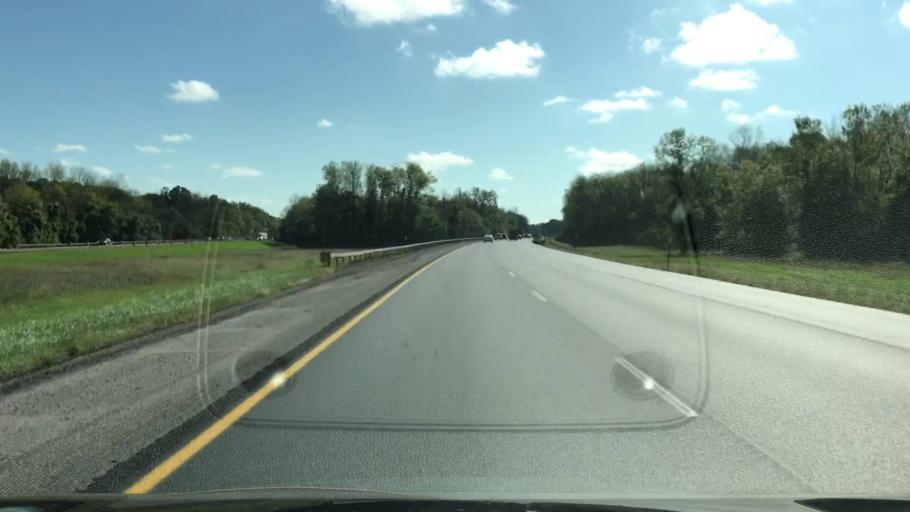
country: US
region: New York
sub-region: Ontario County
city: Manchester
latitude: 42.9776
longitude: -77.2201
